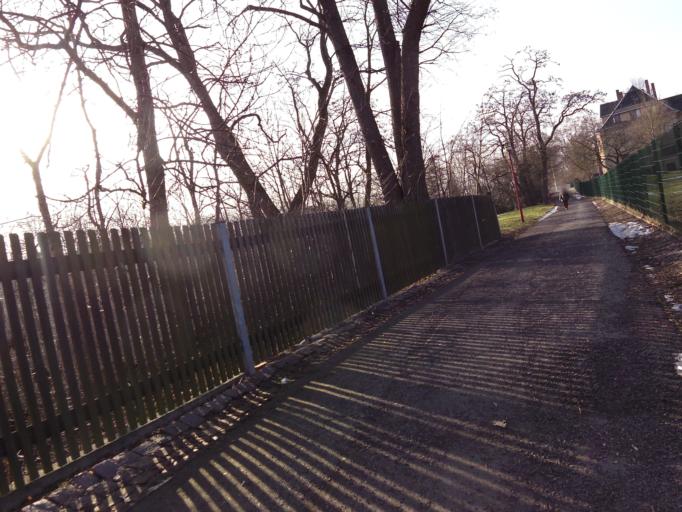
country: DE
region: Saxony
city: Glauchau
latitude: 50.8240
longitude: 12.5461
